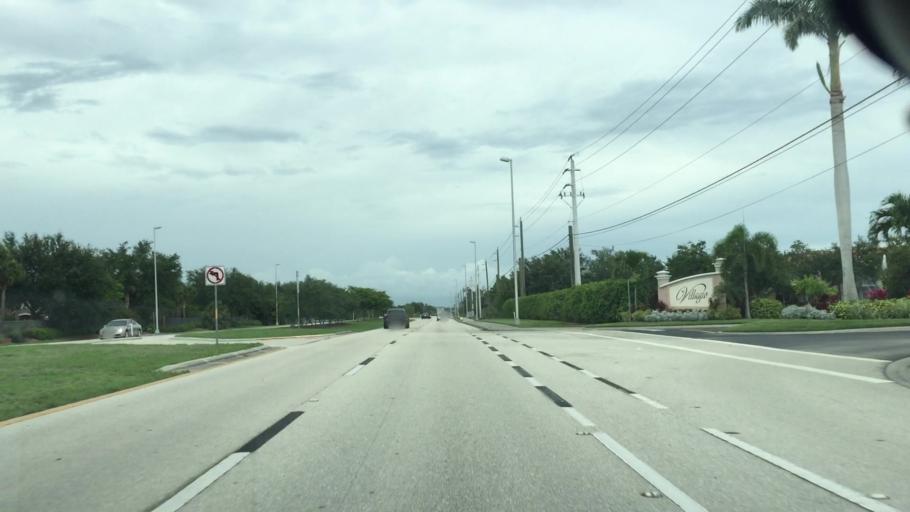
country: US
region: Florida
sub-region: Lee County
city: Estero
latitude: 26.4431
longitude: -81.7886
